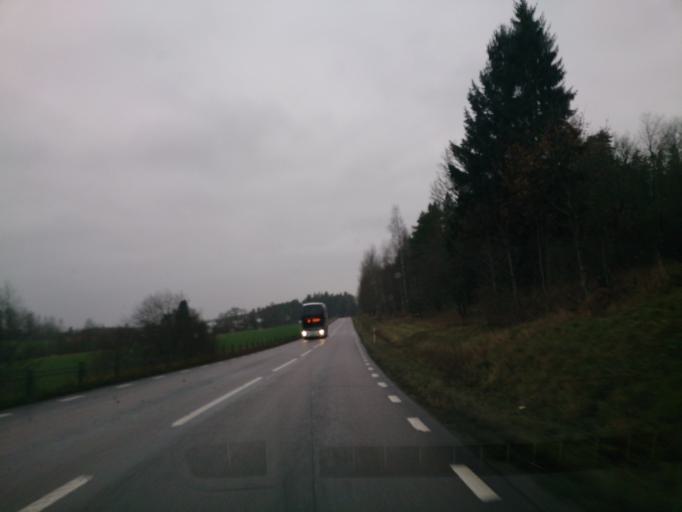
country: SE
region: OEstergoetland
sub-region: Atvidabergs Kommun
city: Atvidaberg
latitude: 58.2809
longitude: 15.9046
